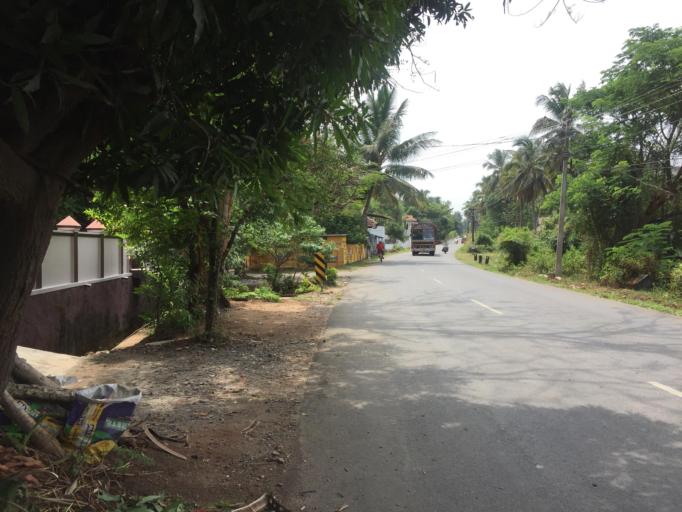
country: IN
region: Kerala
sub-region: Palakkad district
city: Chittur
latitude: 10.6809
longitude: 76.7153
